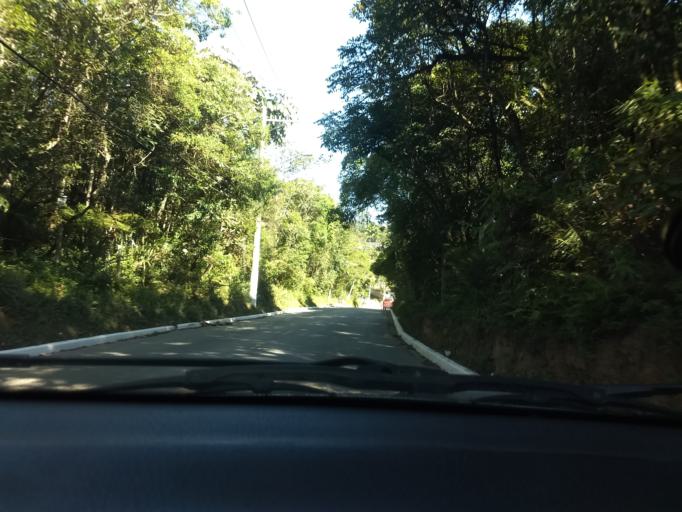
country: BR
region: Sao Paulo
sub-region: Embu-Guacu
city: Embu Guacu
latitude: -23.8113
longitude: -46.7523
